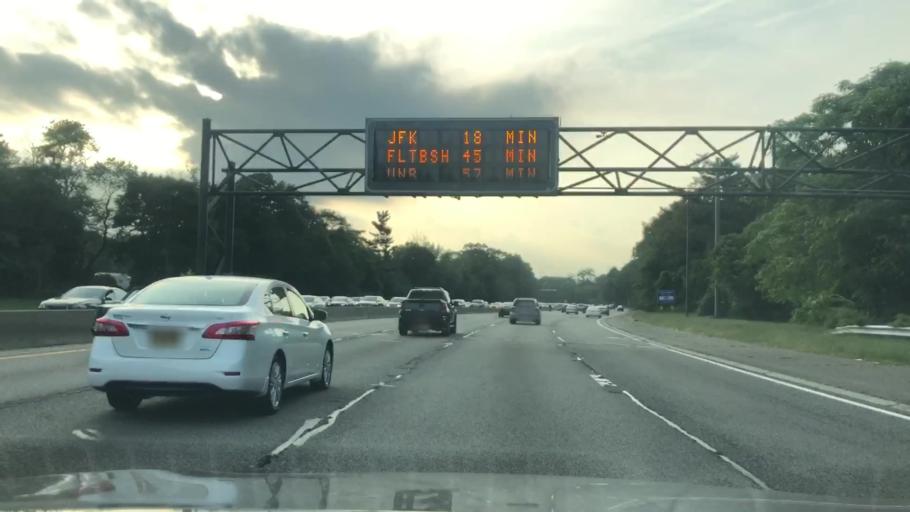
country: US
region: New York
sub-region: Nassau County
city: Malverne
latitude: 40.6830
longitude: -73.6739
